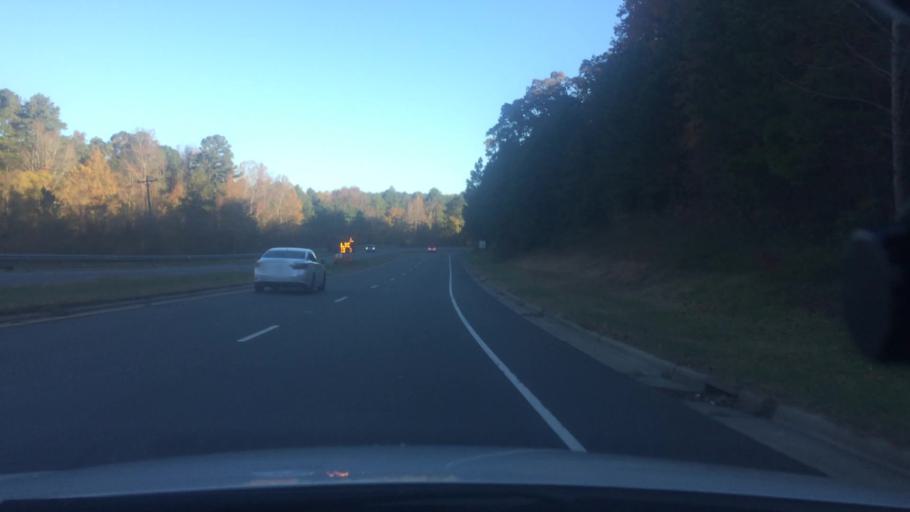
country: US
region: North Carolina
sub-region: Orange County
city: Chapel Hill
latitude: 35.8877
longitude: -79.0615
